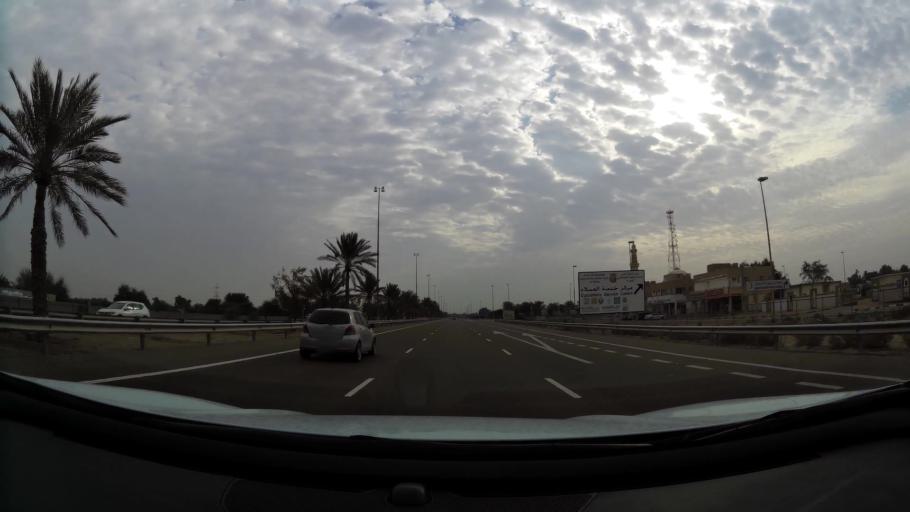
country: AE
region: Abu Dhabi
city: Al Ain
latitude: 24.1709
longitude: 55.1093
